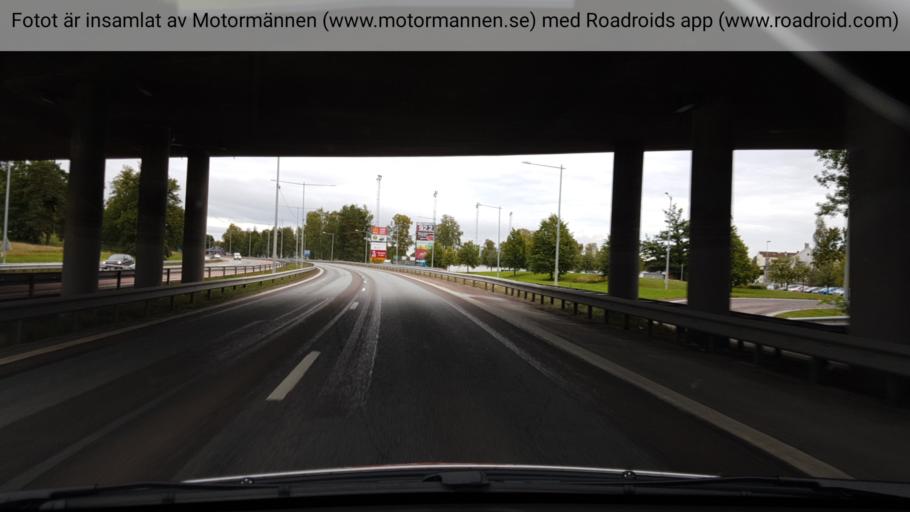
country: SE
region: Vaermland
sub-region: Karlstads Kommun
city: Karlstad
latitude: 59.3848
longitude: 13.4879
